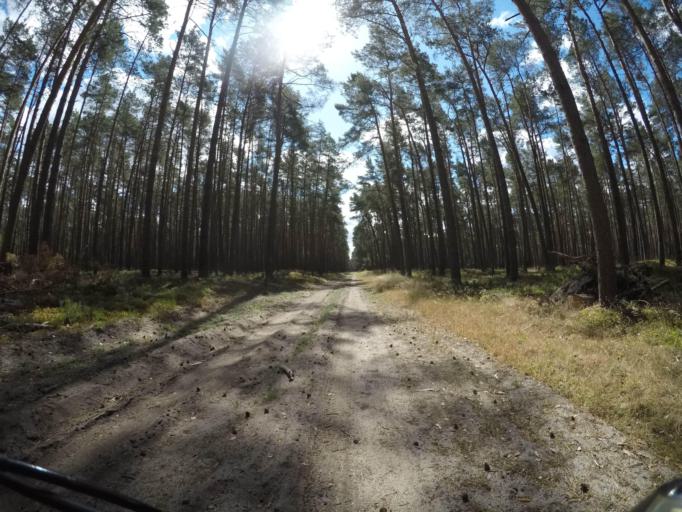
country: DE
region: Lower Saxony
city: Hitzacker
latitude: 53.2163
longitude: 11.0464
